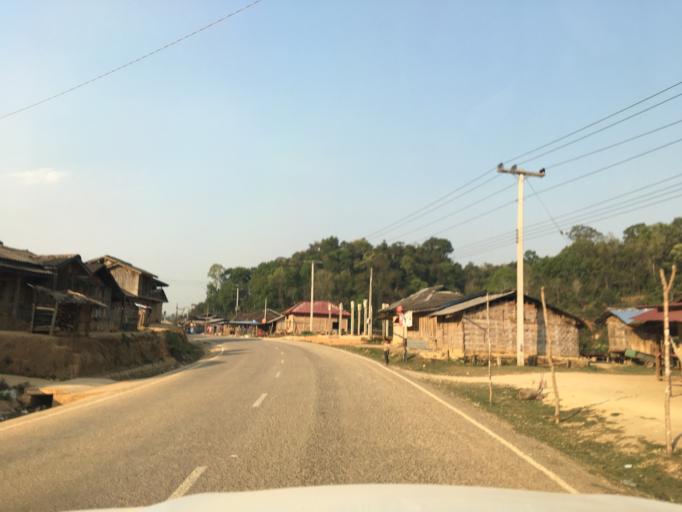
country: LA
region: Houaphan
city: Xam Nua
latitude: 20.5947
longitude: 104.0677
